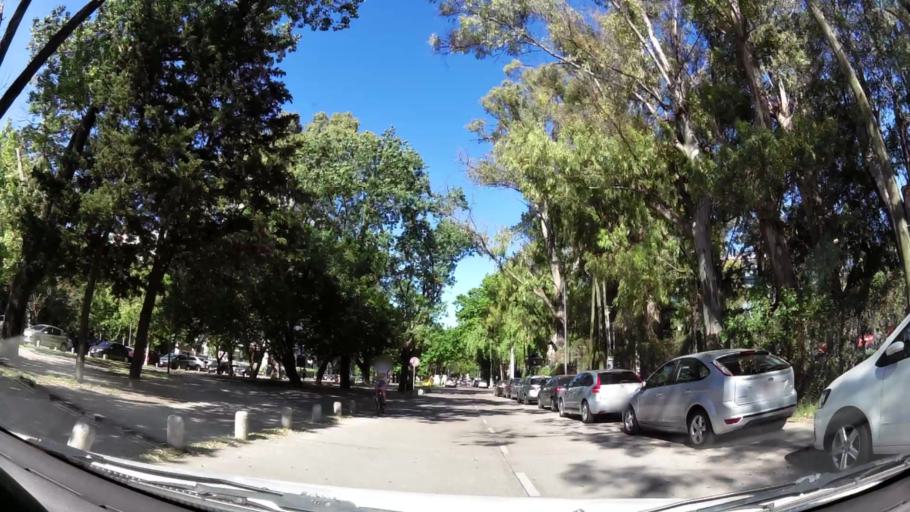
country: AR
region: Buenos Aires
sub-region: Partido de Vicente Lopez
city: Olivos
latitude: -34.5156
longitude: -58.4733
